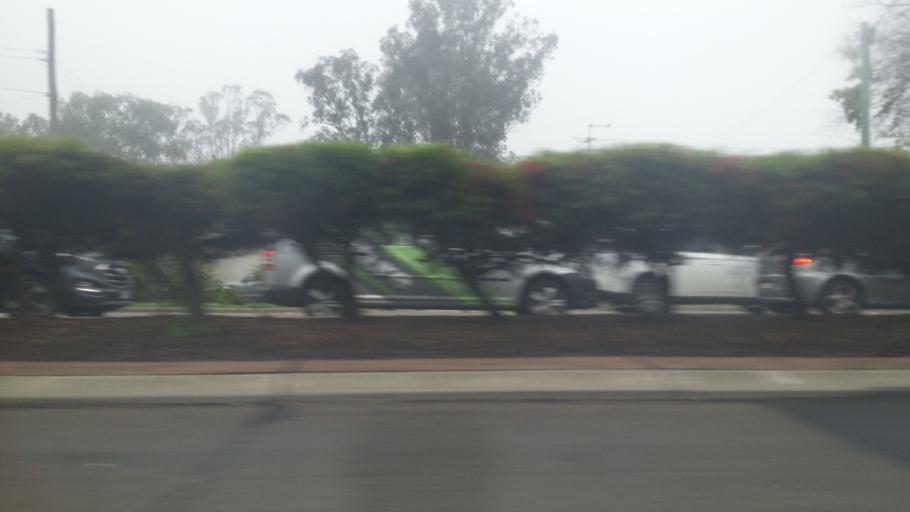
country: AU
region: New South Wales
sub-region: Penrith Municipality
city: Cambridge Park
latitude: -33.7462
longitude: 150.7145
